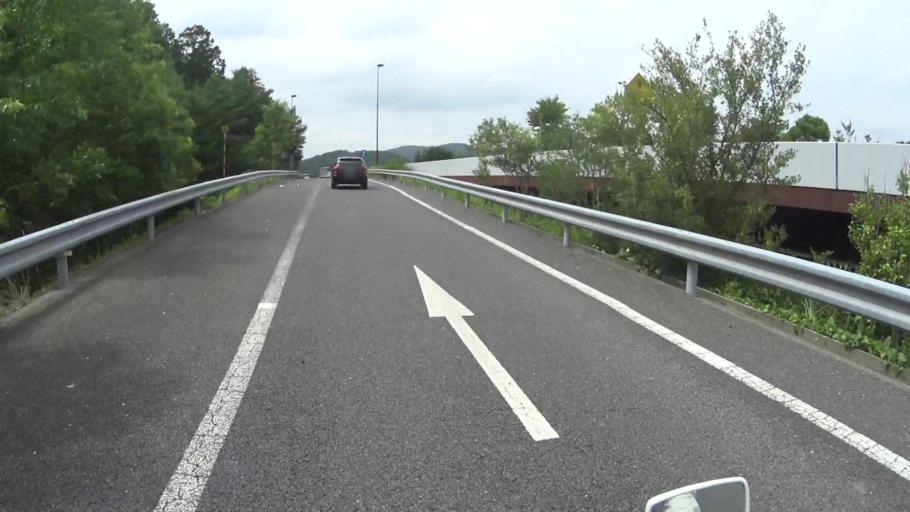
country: JP
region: Kyoto
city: Kameoka
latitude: 35.0802
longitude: 135.5121
